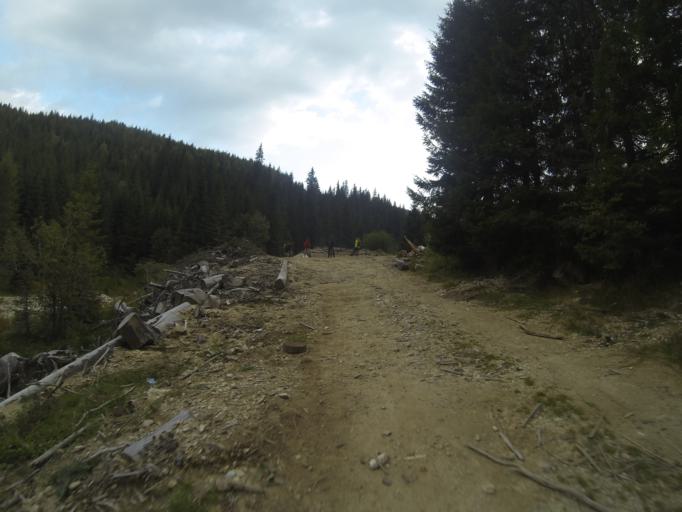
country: RO
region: Gorj
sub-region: Comuna Polovragi
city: Polovragi
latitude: 45.2861
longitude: 23.8418
